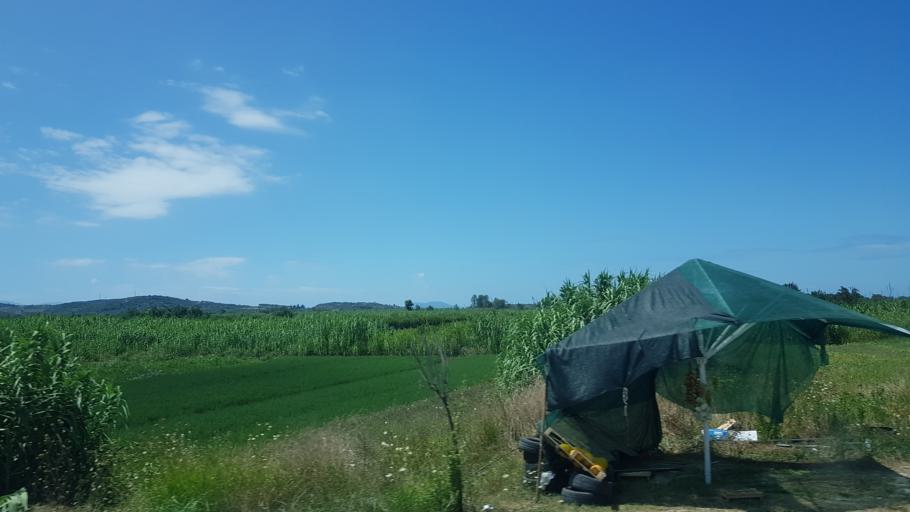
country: AL
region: Fier
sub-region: Rrethi i Fierit
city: Frakulla e Madhe
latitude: 40.6226
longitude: 19.5154
